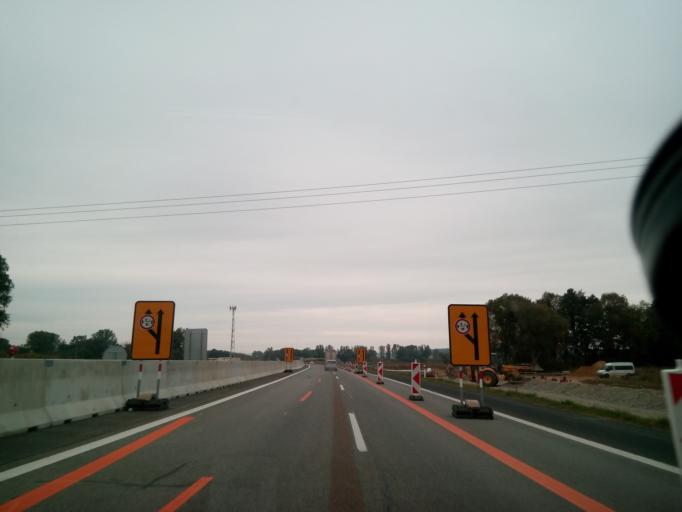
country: SK
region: Kosicky
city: Kosice
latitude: 48.8307
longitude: 21.3075
